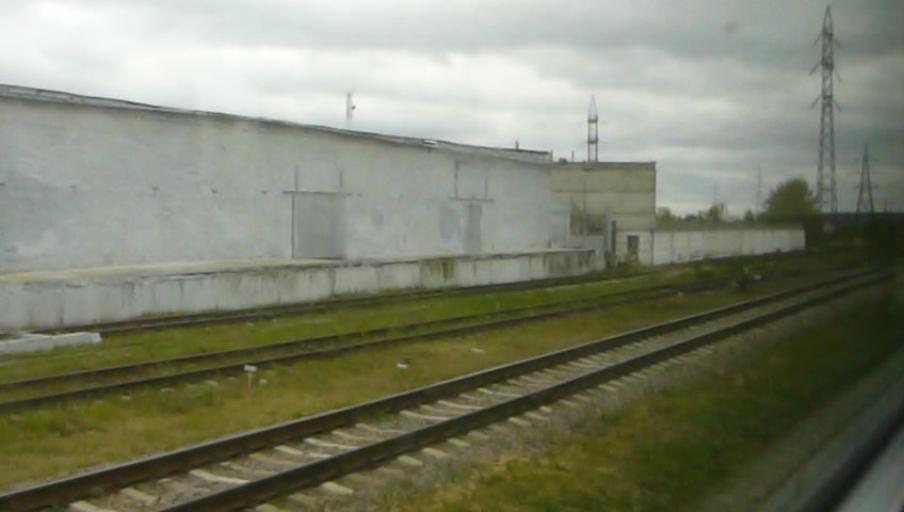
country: RU
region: Moskovskaya
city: Yegor'yevsk
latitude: 55.3954
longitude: 39.0047
